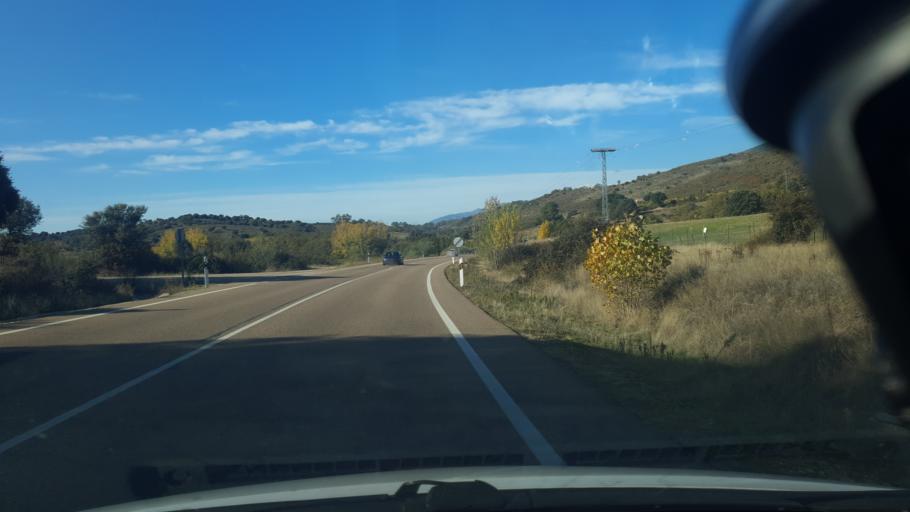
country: ES
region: Castille and Leon
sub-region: Provincia de Avila
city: Poyales del Hoyo
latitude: 40.1583
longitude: -5.1546
